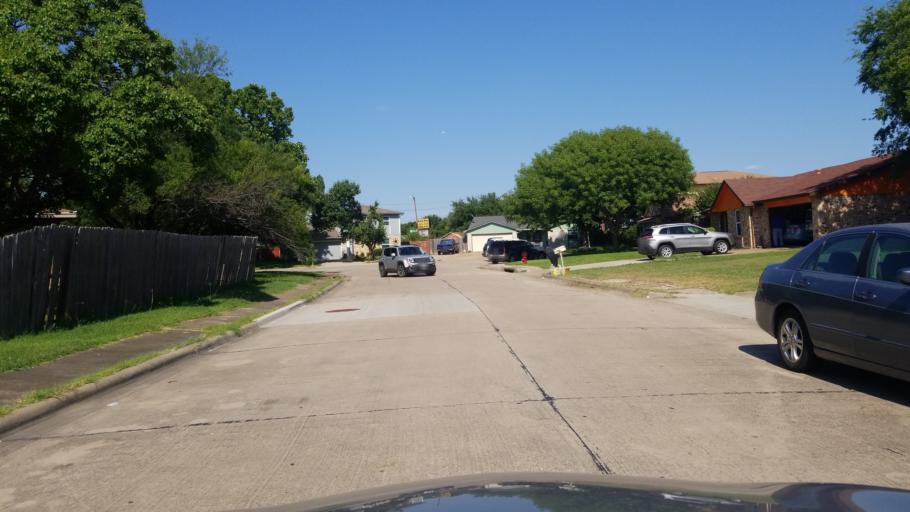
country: US
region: Texas
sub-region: Dallas County
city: Grand Prairie
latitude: 32.6858
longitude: -97.0146
